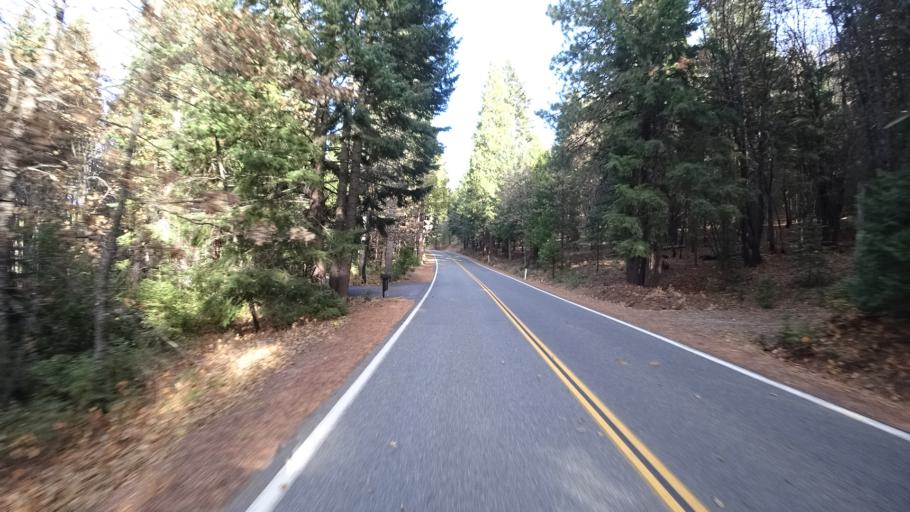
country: US
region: California
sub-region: Siskiyou County
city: Weed
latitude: 41.4063
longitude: -122.4020
